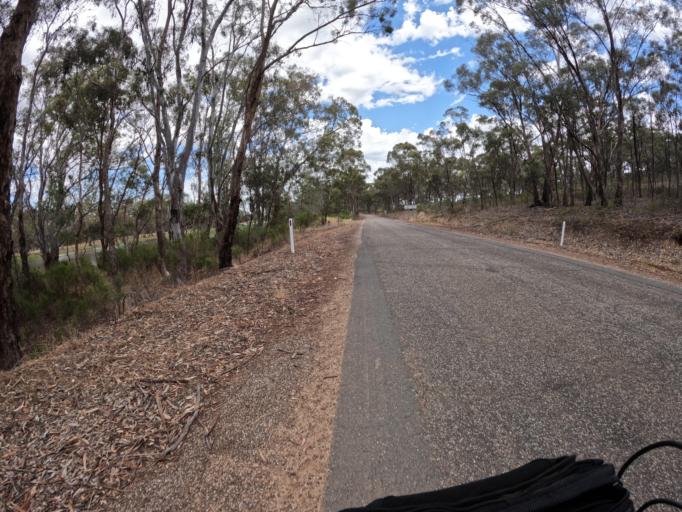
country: AU
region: Victoria
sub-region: Greater Shepparton
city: Shepparton
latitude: -36.6910
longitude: 145.1768
